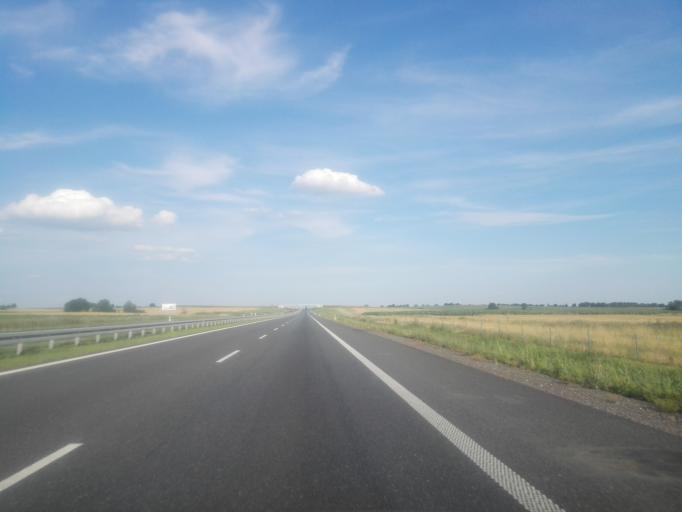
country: PL
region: Lower Silesian Voivodeship
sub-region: Powiat olesnicki
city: Sycow
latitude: 51.3012
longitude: 17.6423
